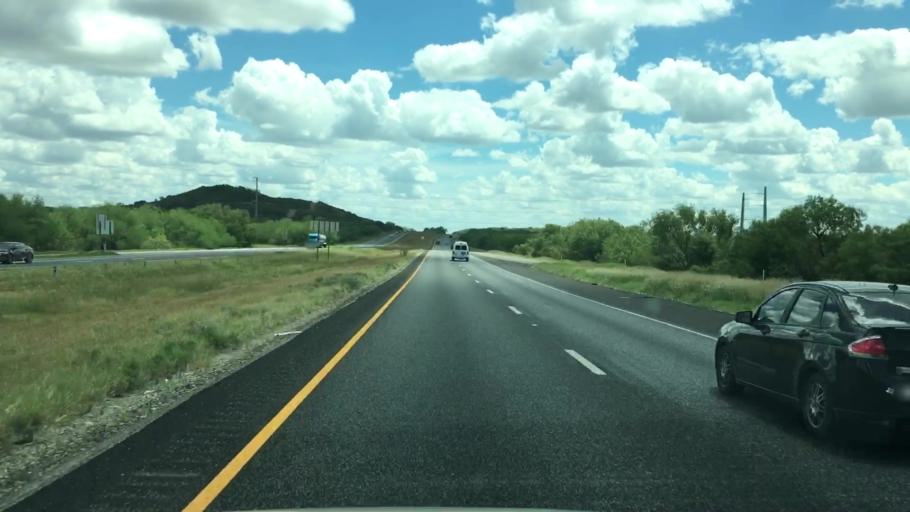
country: US
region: Texas
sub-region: Live Oak County
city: Three Rivers
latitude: 28.7290
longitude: -98.2877
